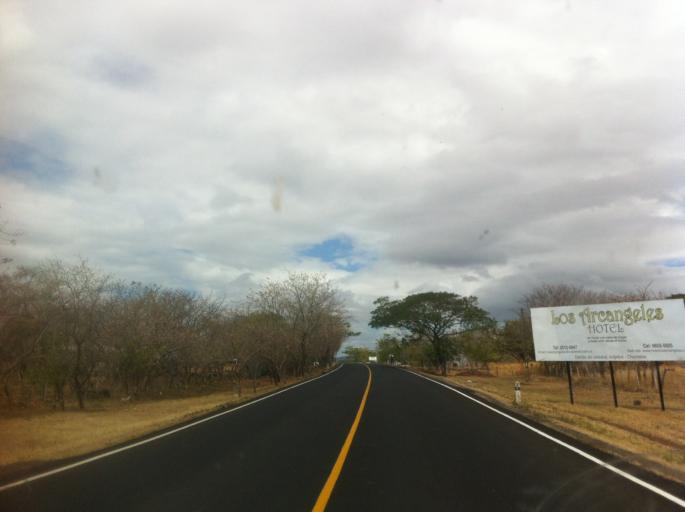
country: NI
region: Chontales
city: Juigalpa
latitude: 12.0890
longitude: -85.3426
